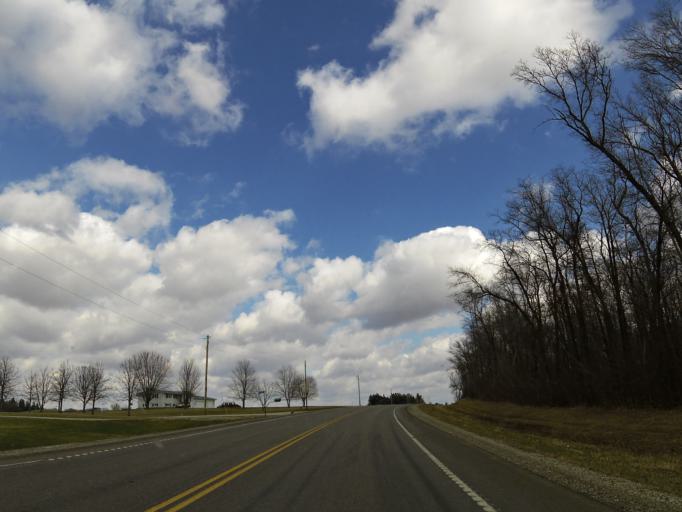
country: US
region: Minnesota
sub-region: Olmsted County
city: Byron
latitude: 44.0831
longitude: -92.6866
